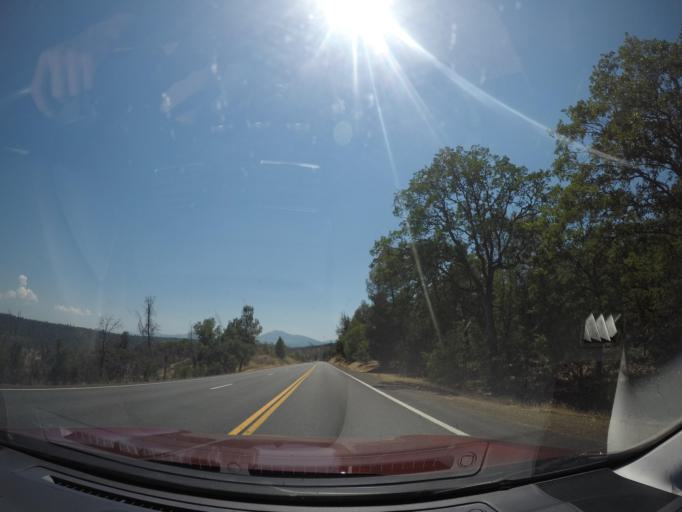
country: US
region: California
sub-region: Shasta County
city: Burney
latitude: 40.9998
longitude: -121.5088
